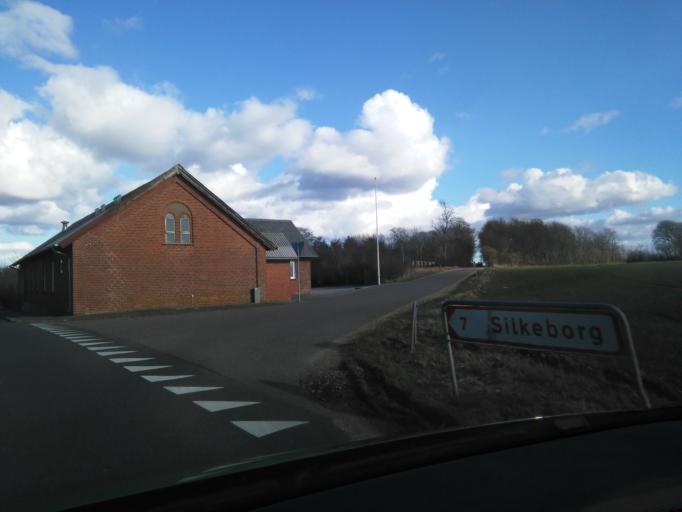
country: DK
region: Central Jutland
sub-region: Silkeborg Kommune
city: Silkeborg
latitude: 56.1915
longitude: 9.4727
